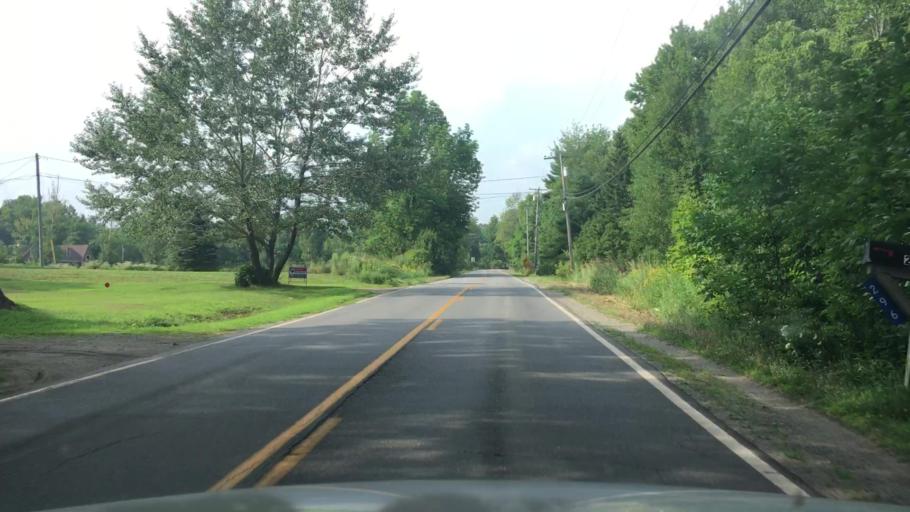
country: US
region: Maine
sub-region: Lincoln County
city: Waldoboro
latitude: 44.1110
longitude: -69.3660
